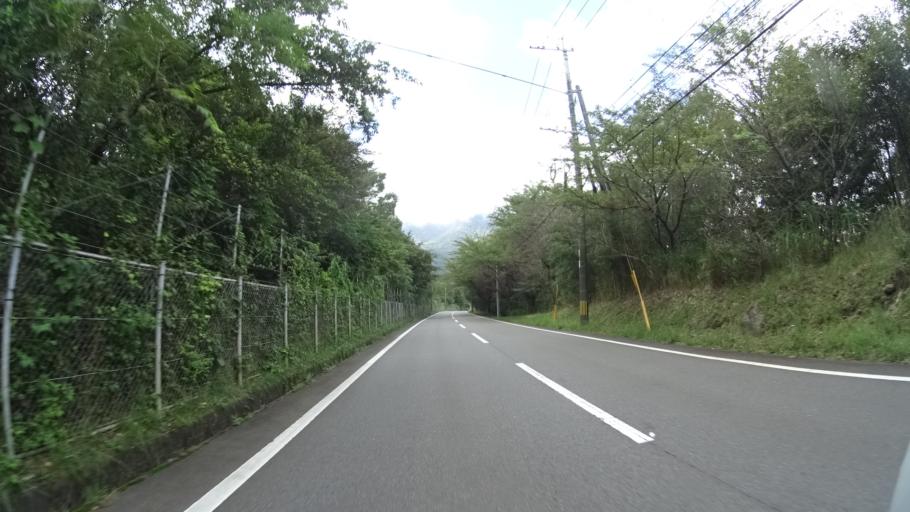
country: JP
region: Oita
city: Beppu
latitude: 33.3084
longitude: 131.4057
